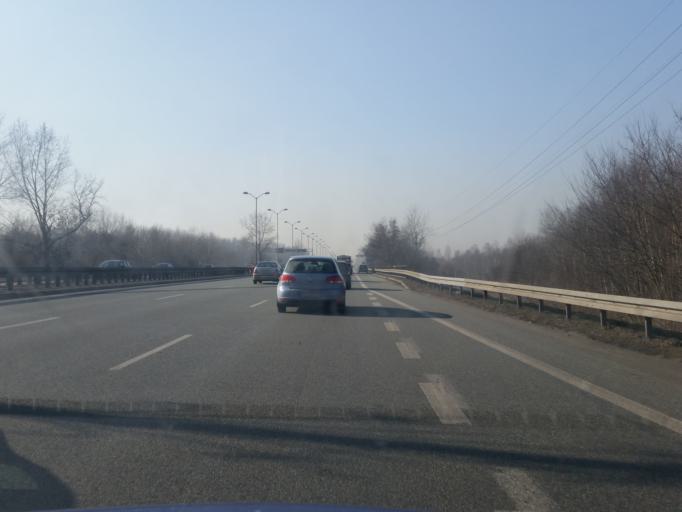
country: PL
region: Silesian Voivodeship
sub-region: Sosnowiec
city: Sosnowiec
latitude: 50.2823
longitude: 19.0917
